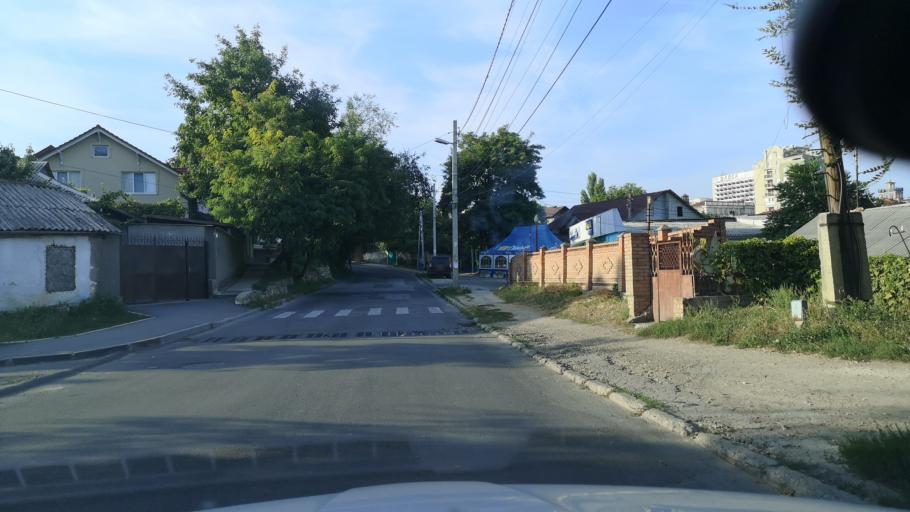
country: MD
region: Chisinau
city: Chisinau
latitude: 47.0103
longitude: 28.8479
